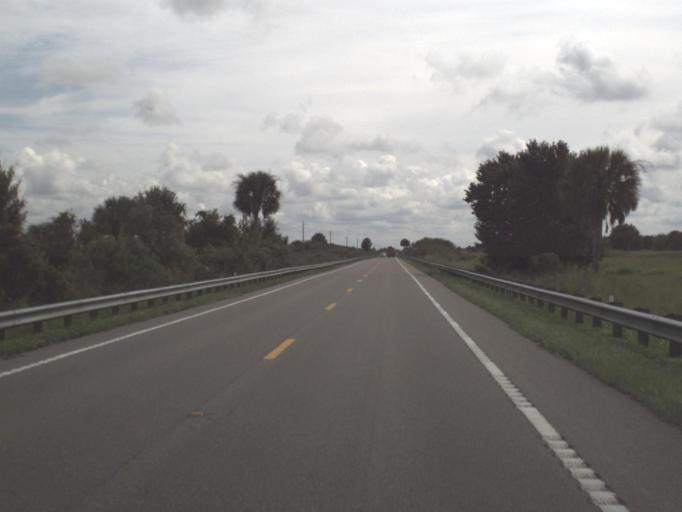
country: US
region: Florida
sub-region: Highlands County
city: Lake Placid
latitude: 27.2095
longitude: -81.1722
